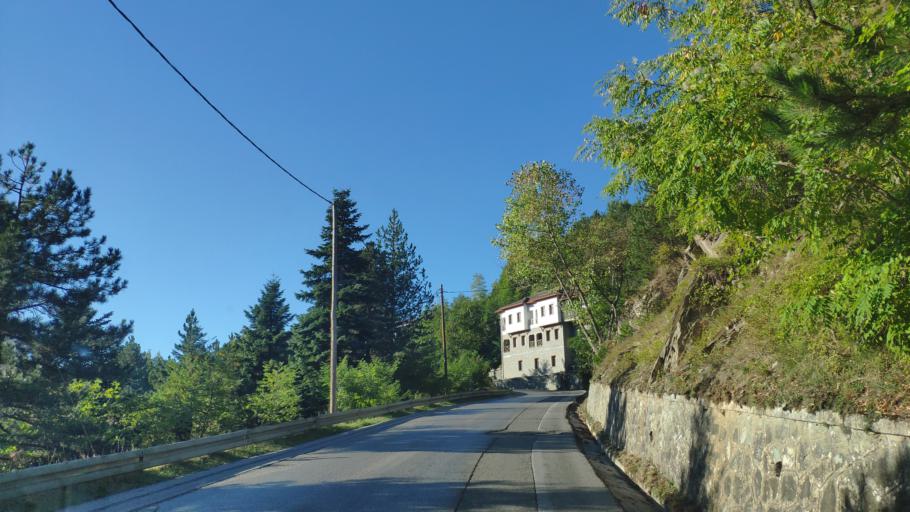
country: GR
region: Epirus
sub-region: Nomos Ioanninon
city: Metsovo
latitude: 39.7745
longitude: 21.1791
